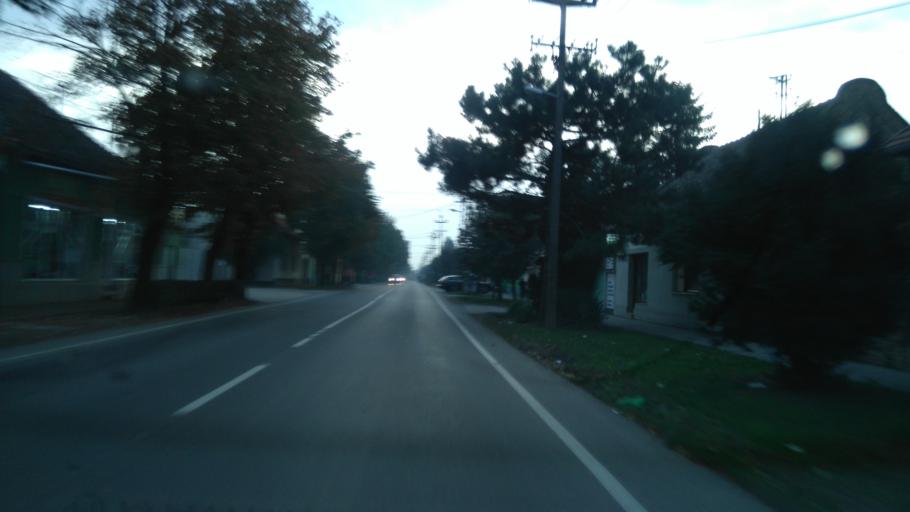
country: RS
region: Autonomna Pokrajina Vojvodina
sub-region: Severnobanatski Okrug
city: Ada
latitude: 45.7937
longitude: 20.1311
